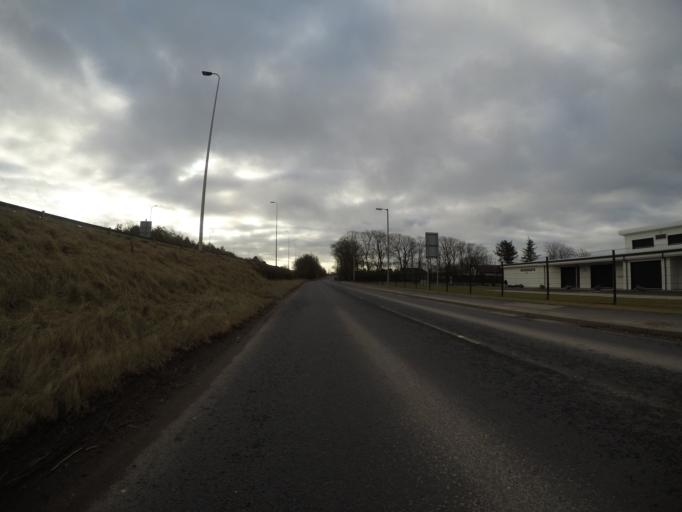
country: GB
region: Scotland
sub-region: North Ayrshire
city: Dreghorn
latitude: 55.5722
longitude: -4.6402
